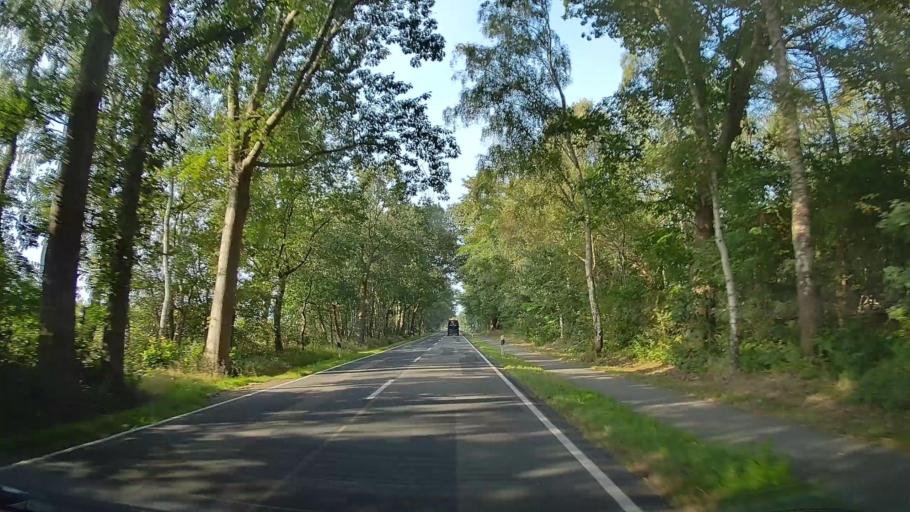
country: DE
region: Lower Saxony
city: Friesoythe
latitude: 53.1016
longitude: 7.8321
